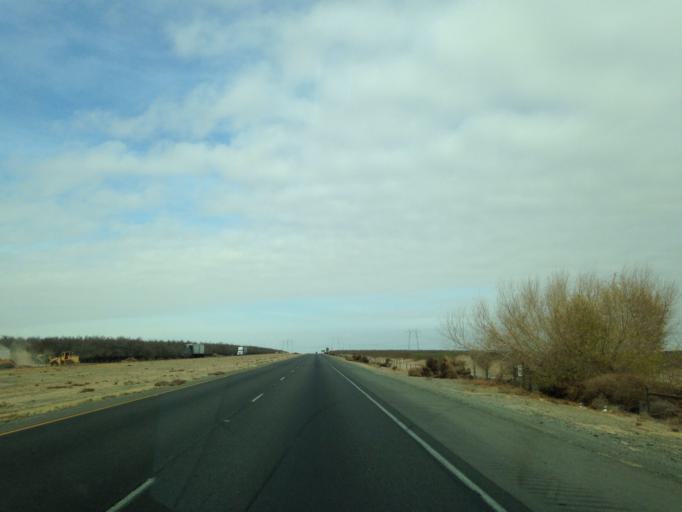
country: US
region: California
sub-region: Fresno County
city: Huron
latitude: 36.2753
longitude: -120.2570
